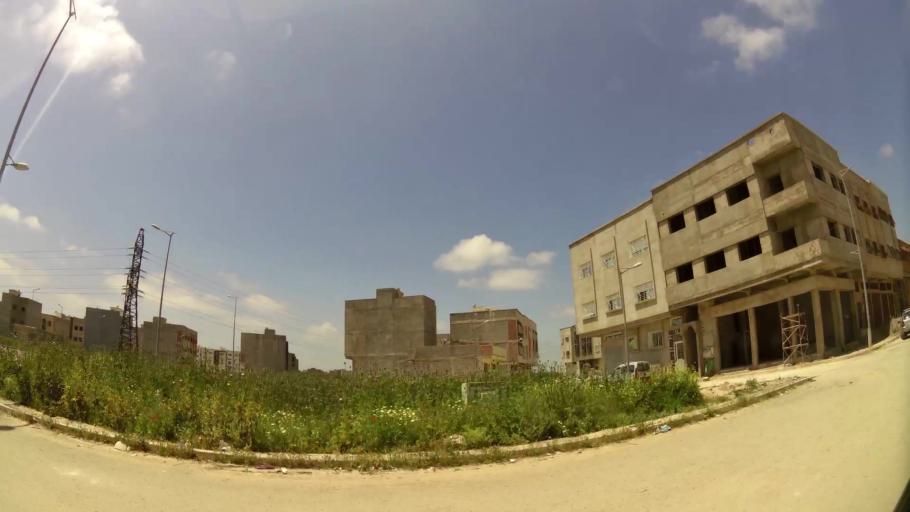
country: MA
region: Fes-Boulemane
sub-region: Fes
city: Fes
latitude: 34.0363
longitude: -5.0565
